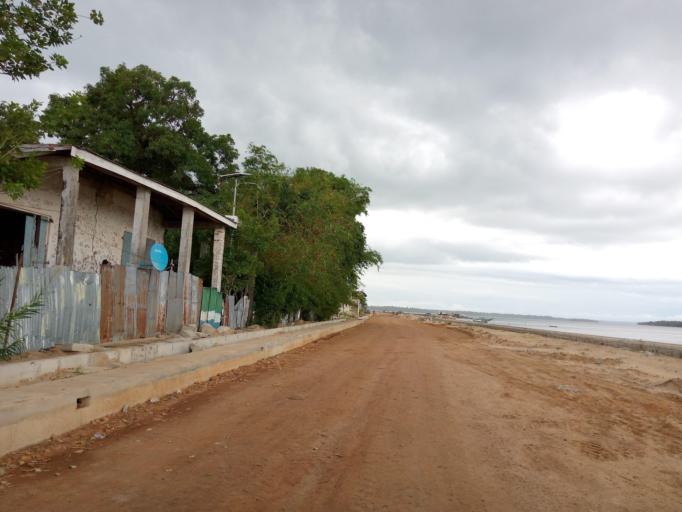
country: SL
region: Southern Province
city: Bonthe
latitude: 7.5271
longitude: -12.5004
